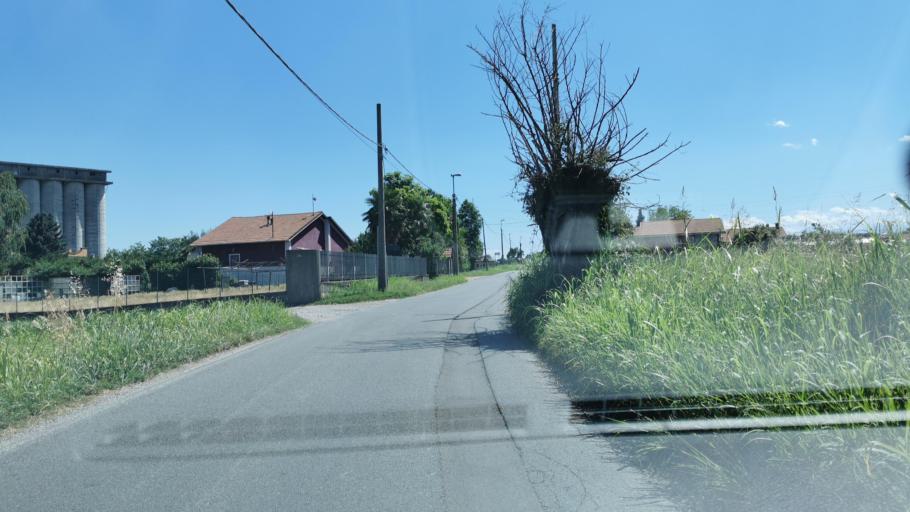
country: IT
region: Piedmont
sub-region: Provincia di Torino
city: Pianezza
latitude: 45.1177
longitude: 7.5632
